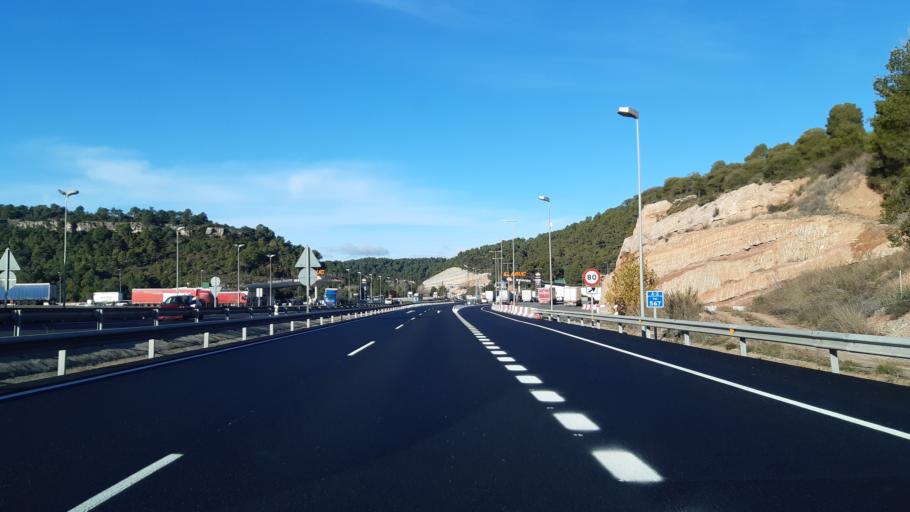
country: ES
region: Catalonia
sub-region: Provincia de Barcelona
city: Castelloli
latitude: 41.5926
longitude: 1.7532
